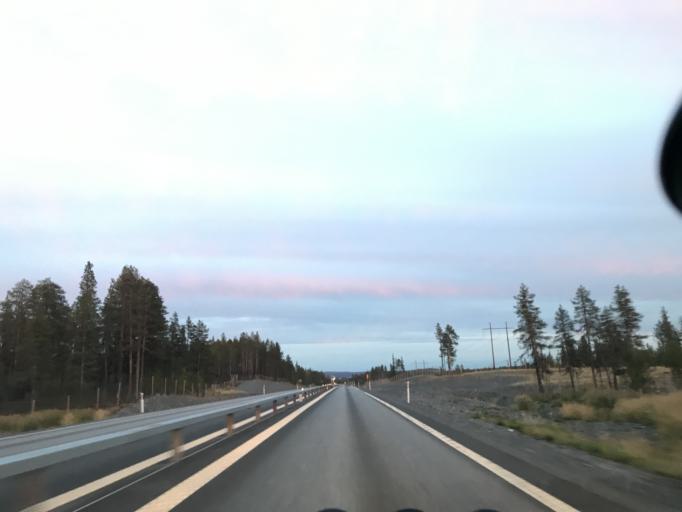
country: SE
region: Norrbotten
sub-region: Gallivare Kommun
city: Malmberget
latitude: 67.6829
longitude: 20.8677
